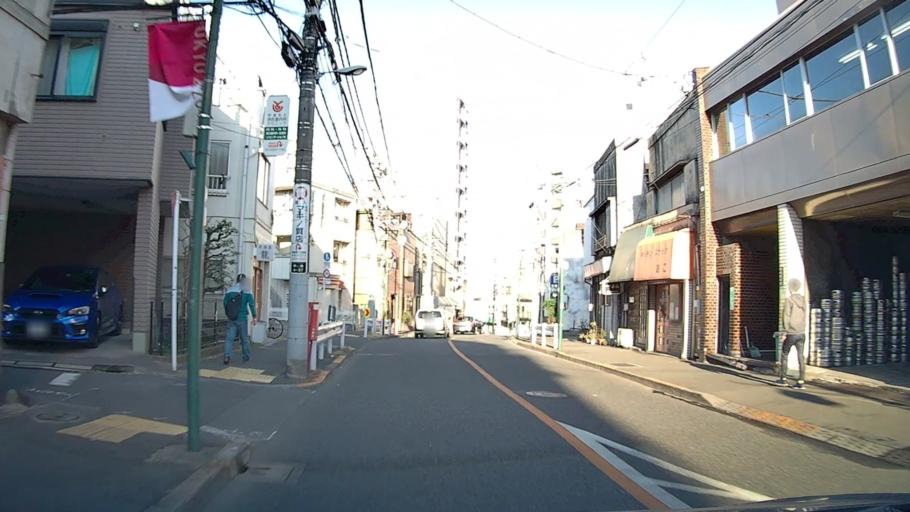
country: JP
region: Tokyo
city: Tokyo
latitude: 35.7003
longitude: 139.6712
